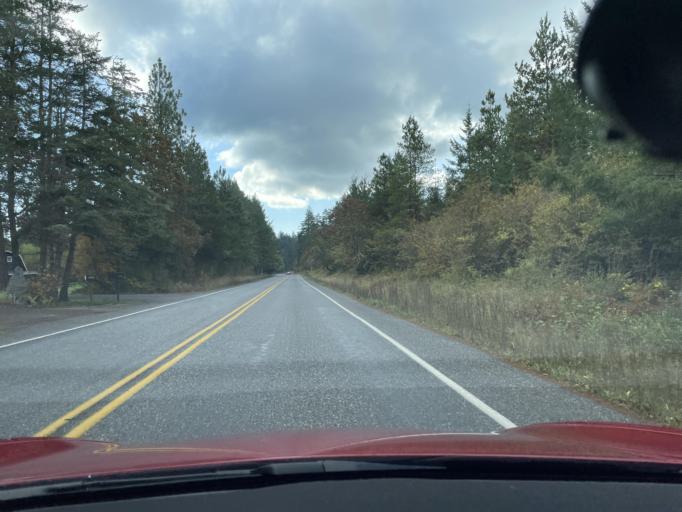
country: US
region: Washington
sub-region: San Juan County
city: Friday Harbor
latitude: 48.5019
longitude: -123.0353
